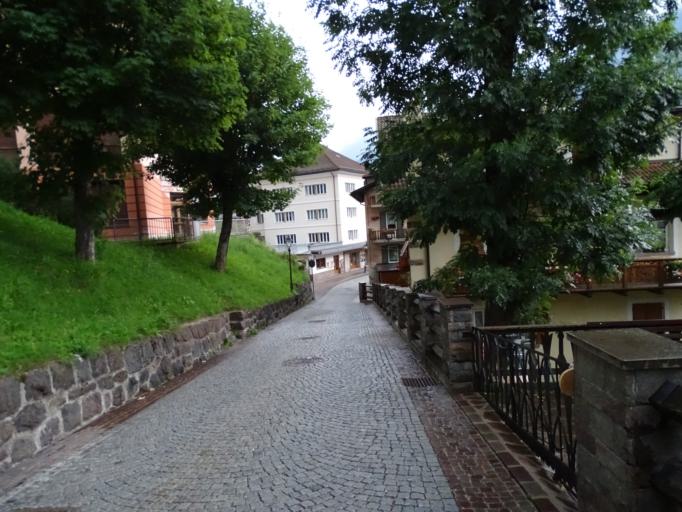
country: IT
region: Trentino-Alto Adige
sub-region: Provincia di Trento
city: Moena
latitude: 46.3759
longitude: 11.6572
